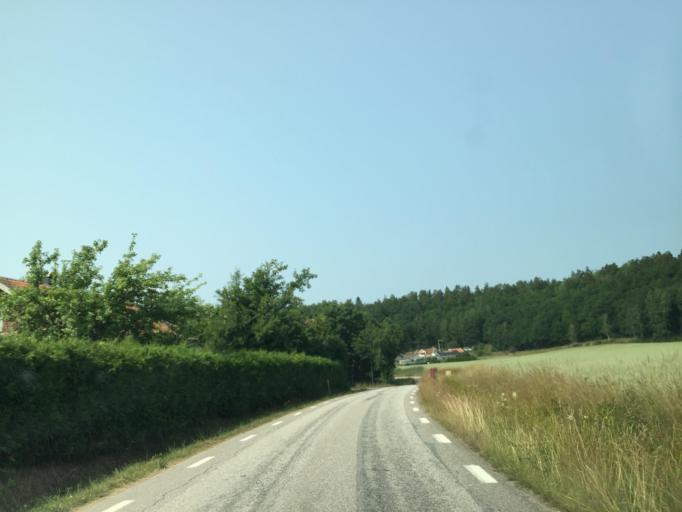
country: SE
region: Vaestra Goetaland
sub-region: Lilla Edets Kommun
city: Lilla Edet
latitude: 58.2124
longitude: 12.1356
